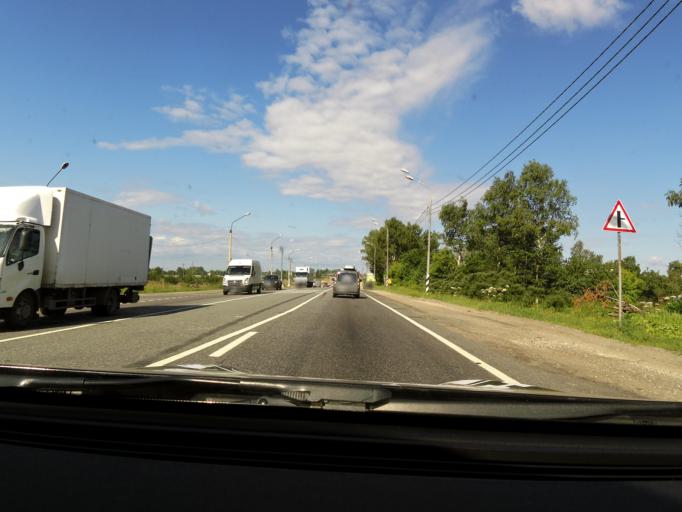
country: RU
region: Tverskaya
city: Tver
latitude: 56.7825
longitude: 35.9625
